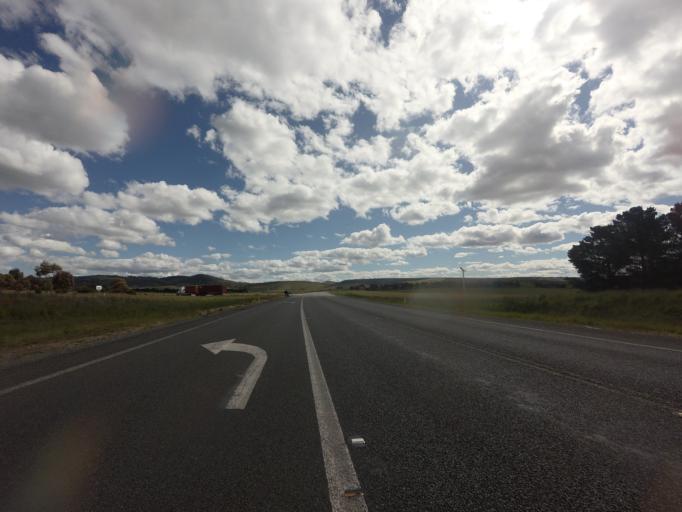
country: AU
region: Tasmania
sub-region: Brighton
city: Bridgewater
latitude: -42.3836
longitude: 147.3155
